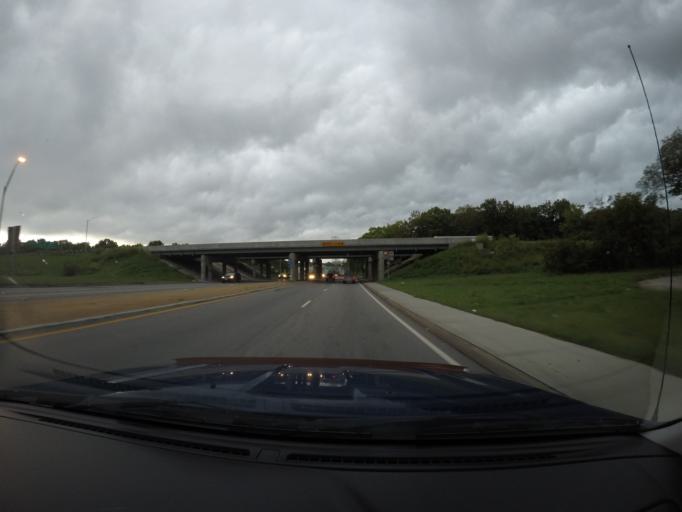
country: US
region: Missouri
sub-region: Jackson County
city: Sugar Creek
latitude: 39.1068
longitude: -94.4854
